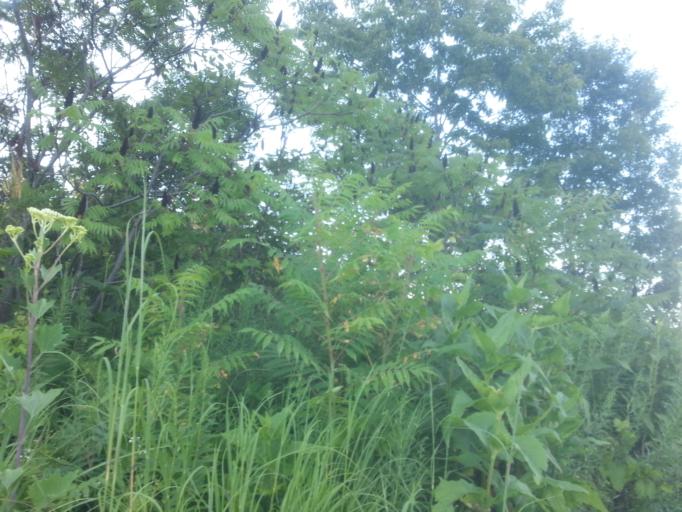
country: US
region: Wisconsin
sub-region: Dane County
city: Middleton
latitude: 43.0723
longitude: -89.4863
